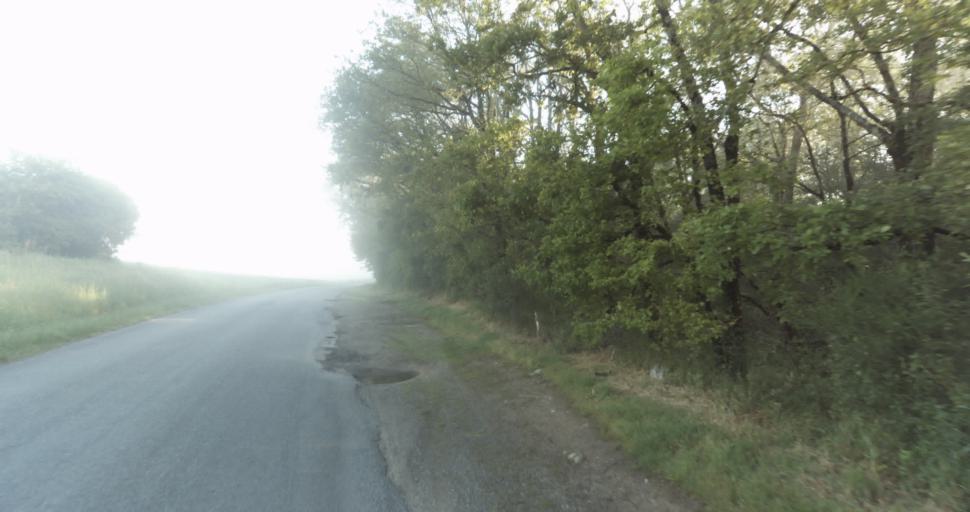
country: FR
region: Limousin
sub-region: Departement de la Haute-Vienne
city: Condat-sur-Vienne
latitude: 45.7847
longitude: 1.3008
